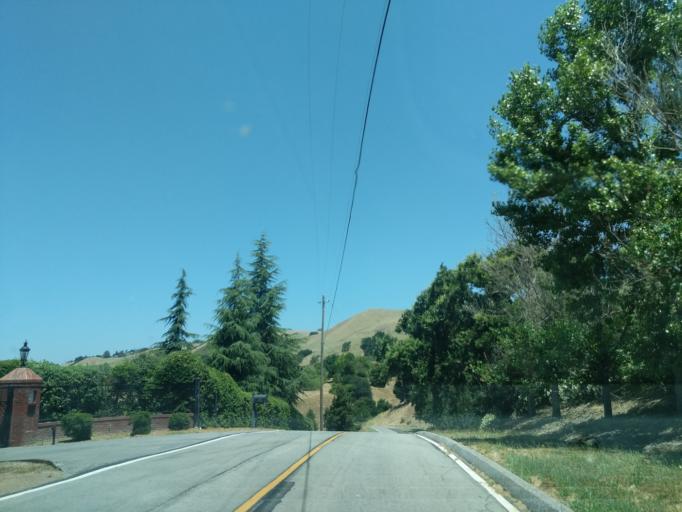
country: US
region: California
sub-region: Santa Clara County
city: San Martin
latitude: 37.1154
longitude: -121.5823
